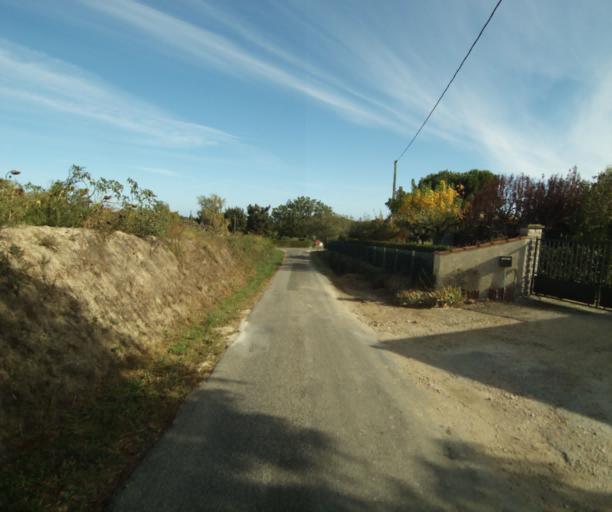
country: FR
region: Midi-Pyrenees
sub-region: Departement du Gers
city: Eauze
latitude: 43.9434
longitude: 0.0986
